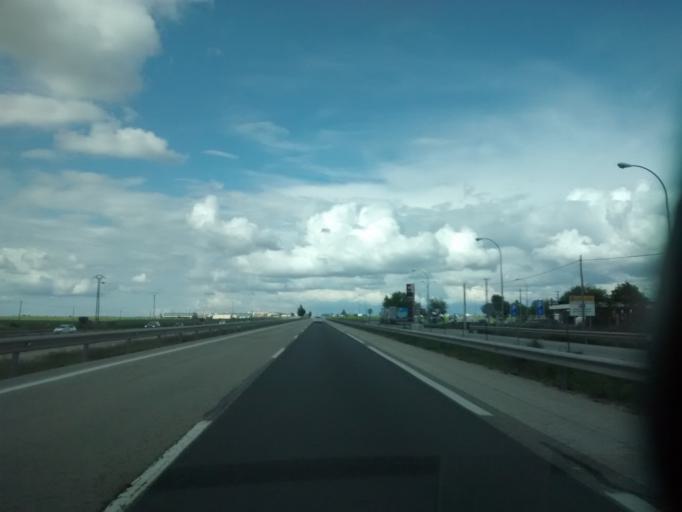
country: ES
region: Castille-La Mancha
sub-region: Provincia de Guadalajara
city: Trijueque
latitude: 40.7610
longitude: -3.0114
